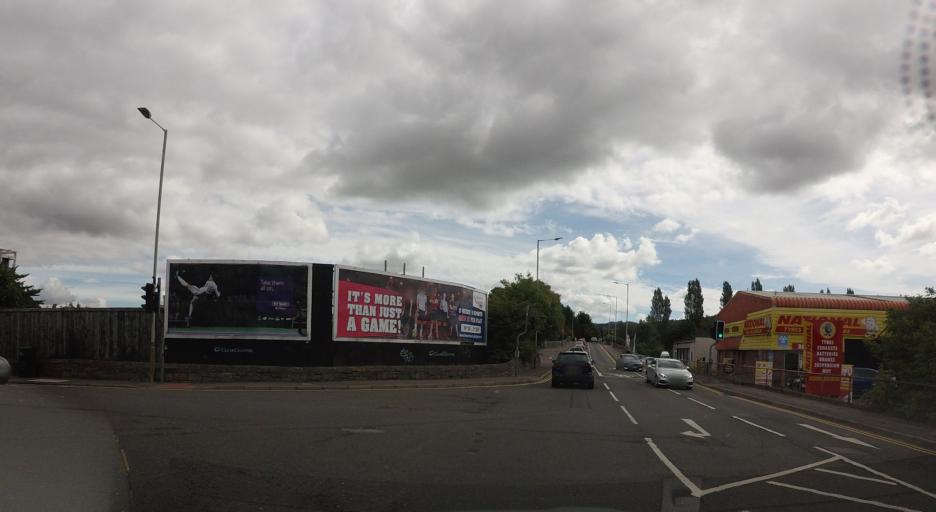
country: GB
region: Scotland
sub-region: Perth and Kinross
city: Perth
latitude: 56.3983
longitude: -3.4453
